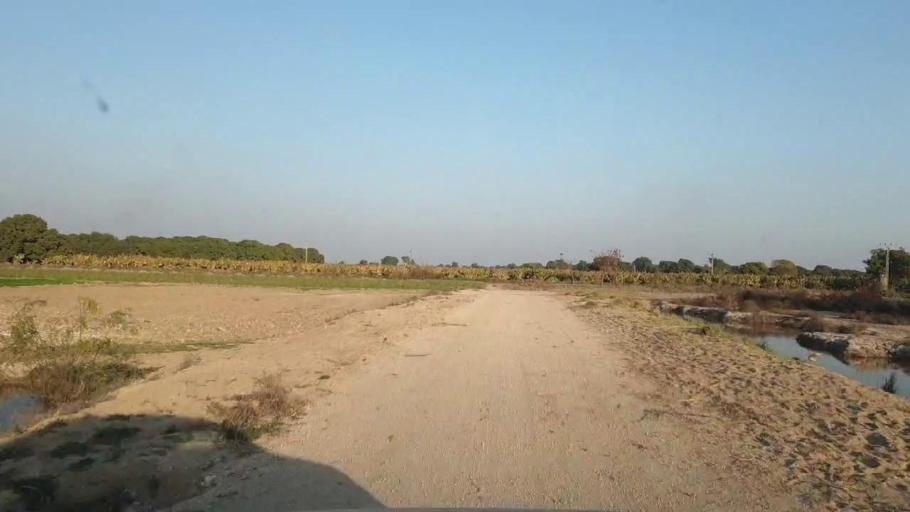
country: PK
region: Sindh
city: Tando Allahyar
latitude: 25.3330
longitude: 68.6831
